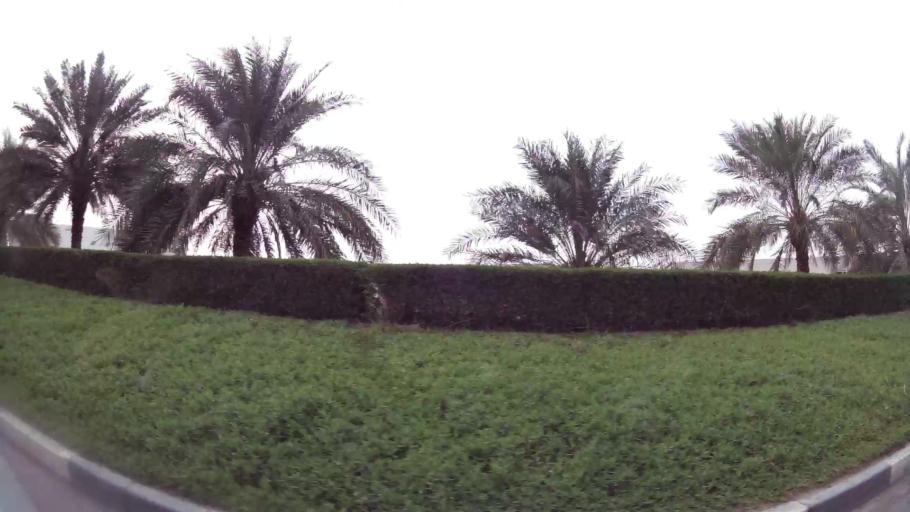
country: AE
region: Abu Dhabi
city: Abu Dhabi
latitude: 24.3456
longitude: 54.5246
